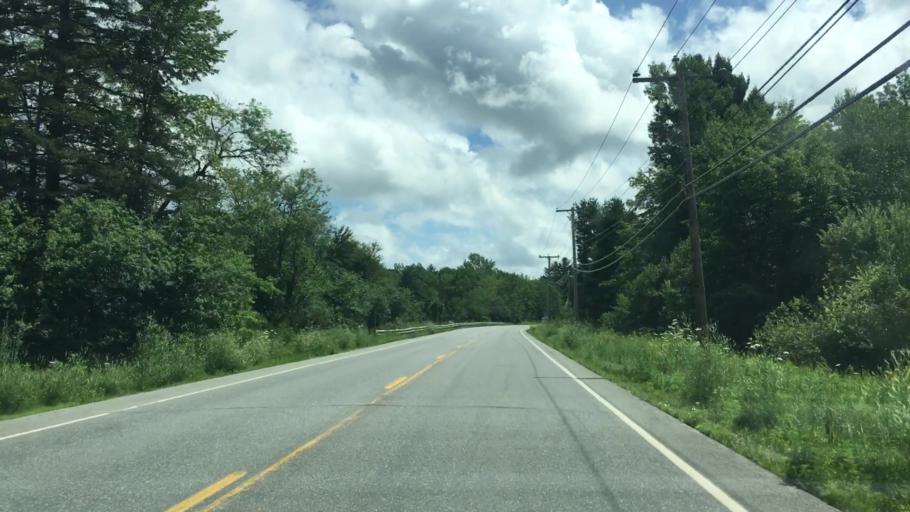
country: US
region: Maine
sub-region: Penobscot County
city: Hermon
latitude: 44.8082
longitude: -68.9735
